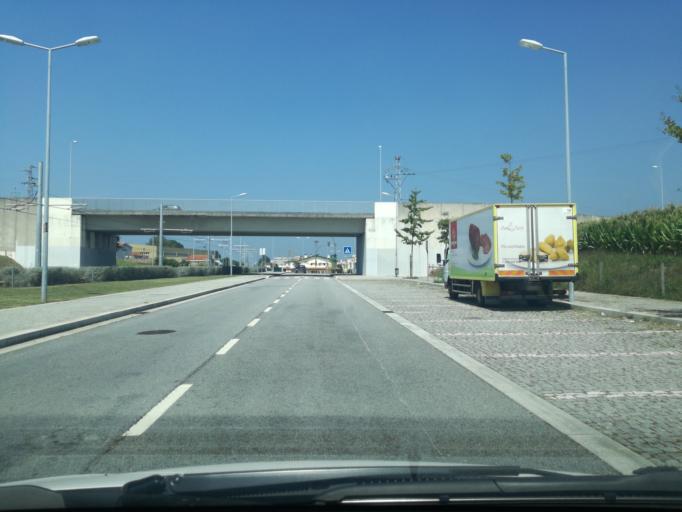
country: PT
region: Porto
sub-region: Matosinhos
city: Santa Cruz do Bispo
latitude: 41.2417
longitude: -8.6592
